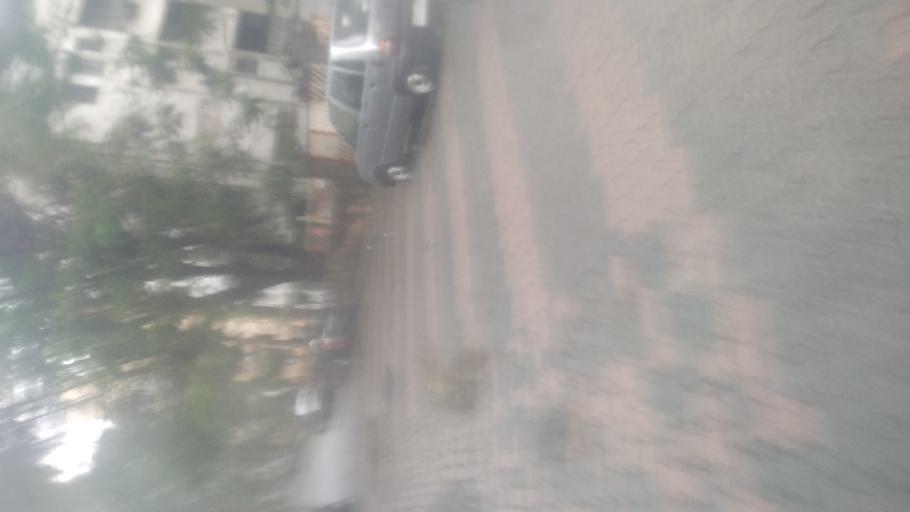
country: IN
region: Maharashtra
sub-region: Mumbai Suburban
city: Borivli
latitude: 19.1720
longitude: 72.8652
